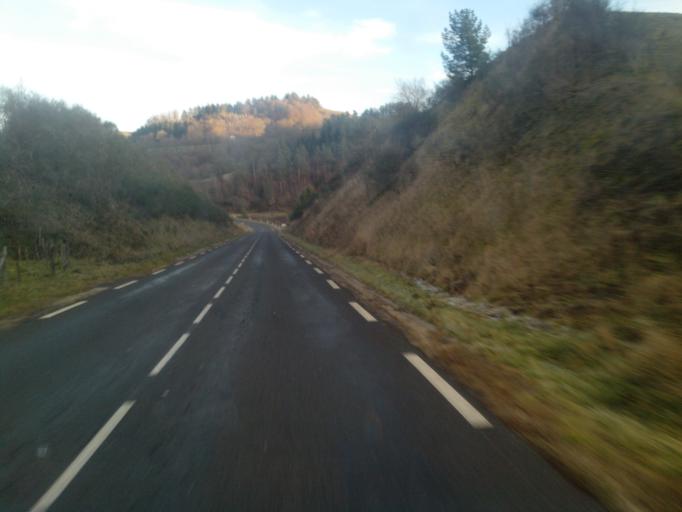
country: FR
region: Auvergne
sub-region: Departement du Cantal
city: Riom-es-Montagnes
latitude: 45.2488
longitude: 2.7065
